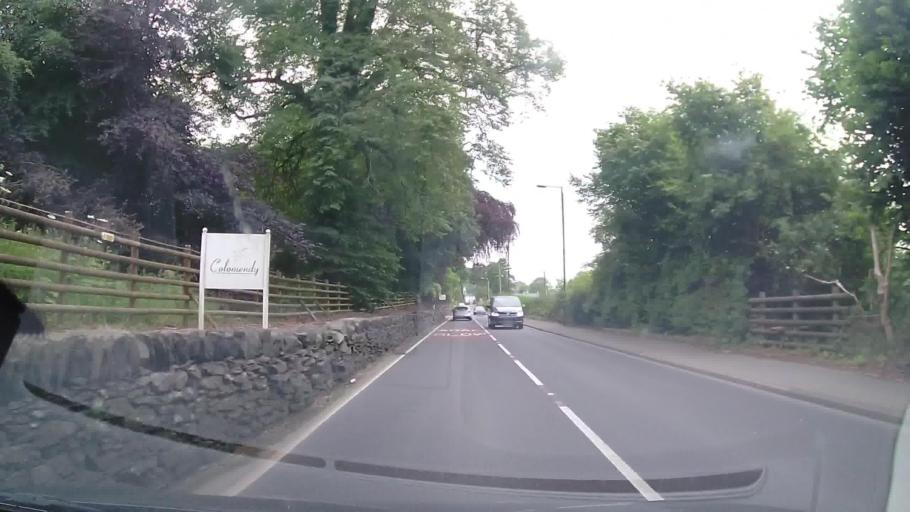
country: GB
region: Wales
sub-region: Denbighshire
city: Corwen
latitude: 52.9812
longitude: -3.3651
